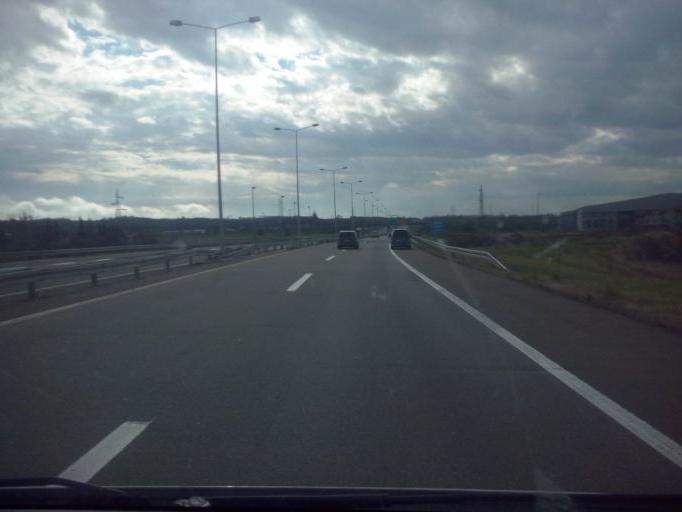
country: RS
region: Central Serbia
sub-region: Pomoravski Okrug
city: Paracin
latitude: 43.8615
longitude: 21.4377
